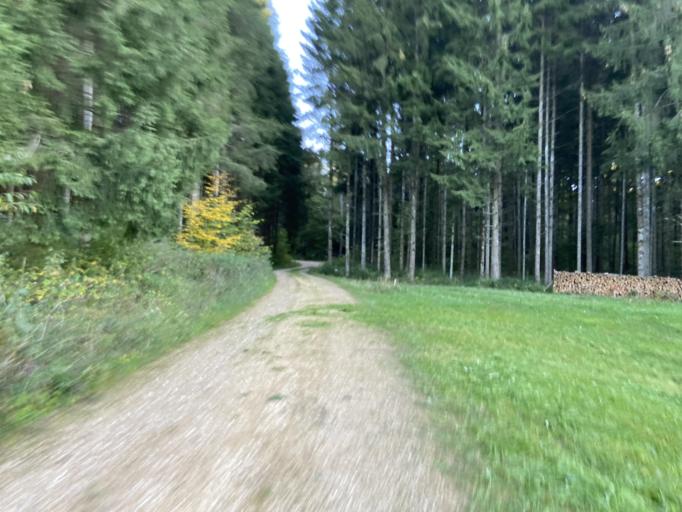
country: DE
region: Baden-Wuerttemberg
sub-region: Tuebingen Region
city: Bingen
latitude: 48.1245
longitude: 9.2779
